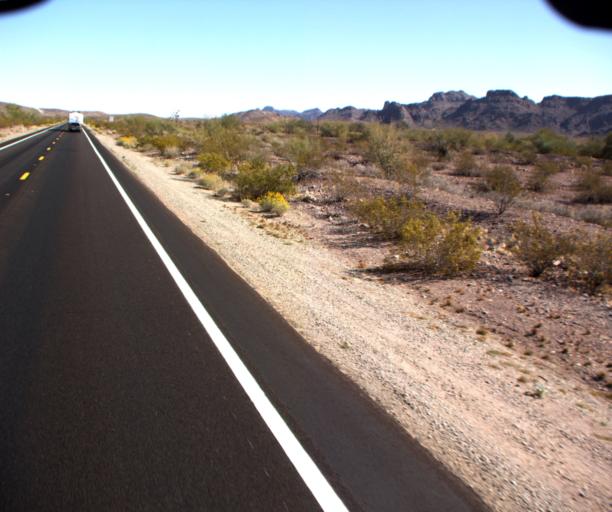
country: US
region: Arizona
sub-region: La Paz County
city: Quartzsite
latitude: 33.2110
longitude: -114.2634
